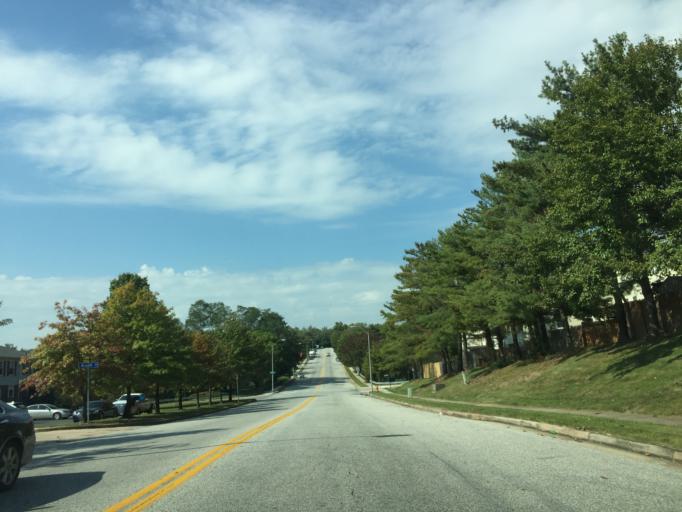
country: US
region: Maryland
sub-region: Baltimore County
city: Carney
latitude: 39.3866
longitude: -76.5026
